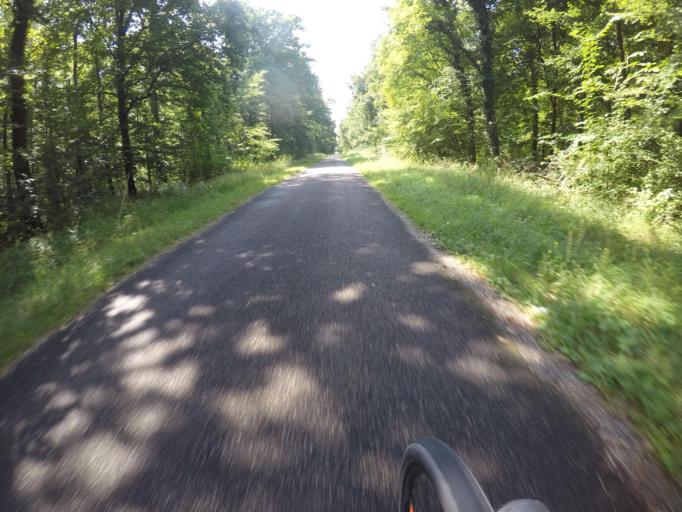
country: DE
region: Baden-Wuerttemberg
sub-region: Karlsruhe Region
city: Forst
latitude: 49.1787
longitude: 8.5958
